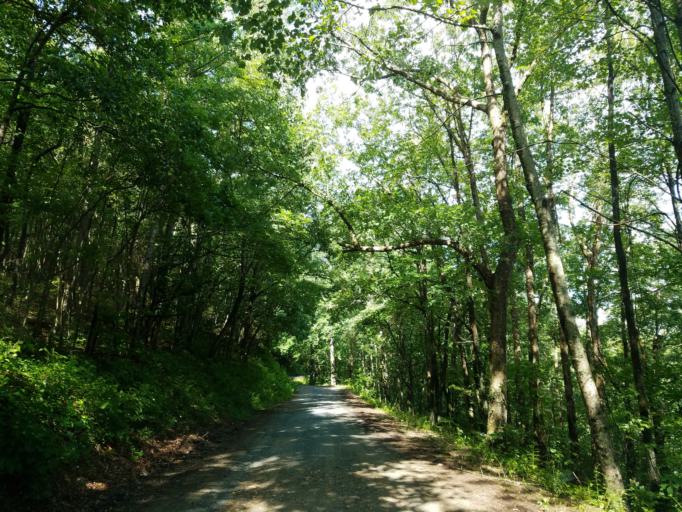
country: US
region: Georgia
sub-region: Fannin County
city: Blue Ridge
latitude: 34.6690
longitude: -84.2466
